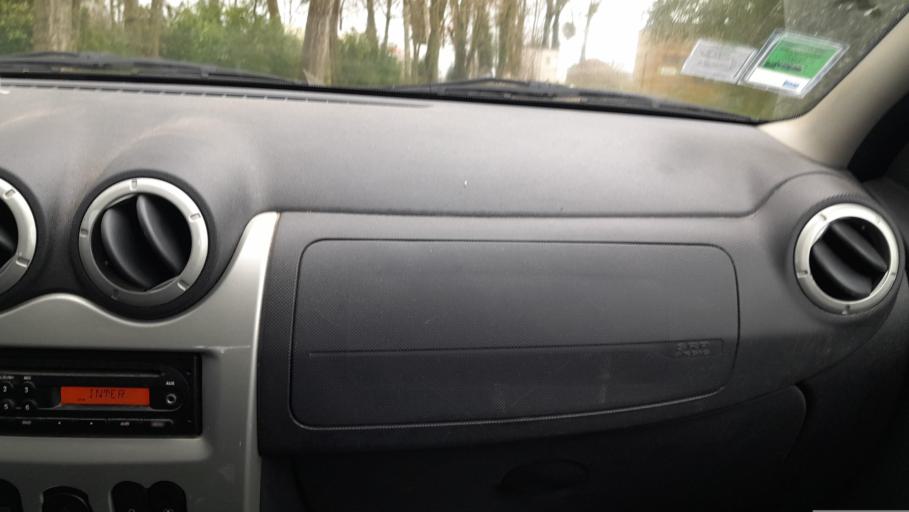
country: FR
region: Brittany
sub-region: Departement d'Ille-et-Vilaine
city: La Guerche-de-Bretagne
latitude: 47.9152
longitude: -1.1547
